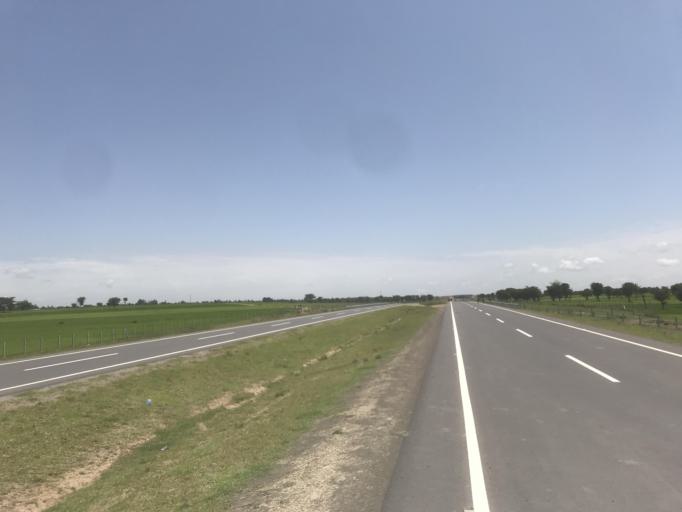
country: ET
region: Oromiya
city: Mojo
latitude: 8.3207
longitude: 38.9546
